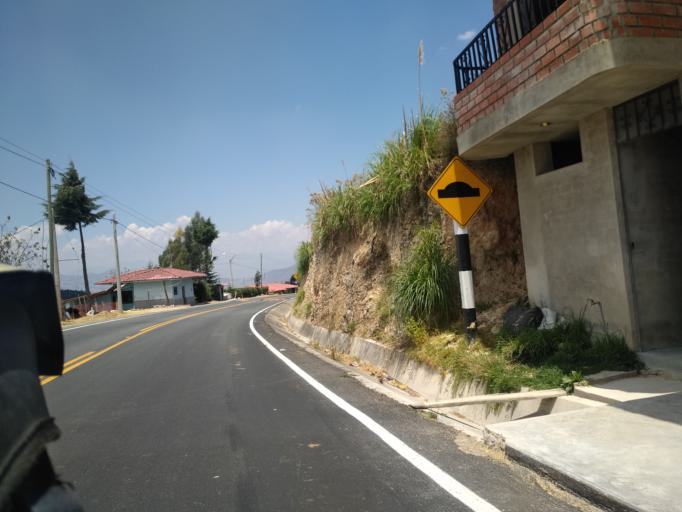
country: PE
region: Cajamarca
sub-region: San Marcos
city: San Marcos
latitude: -7.2773
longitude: -78.2422
